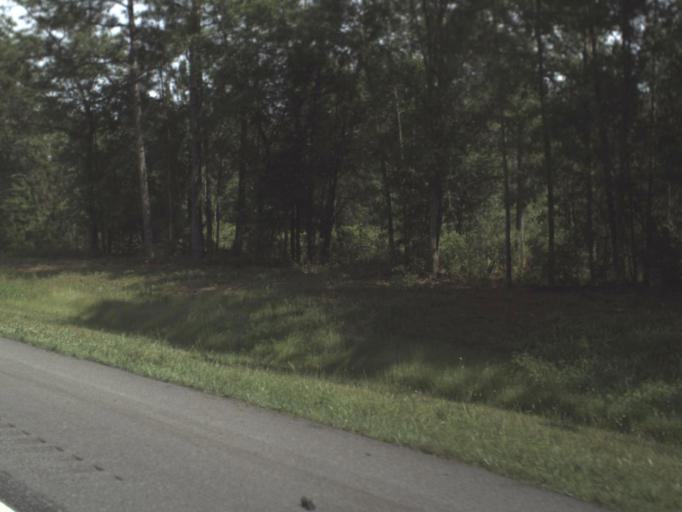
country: US
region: Florida
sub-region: Columbia County
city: Five Points
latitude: 30.2431
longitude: -82.6541
